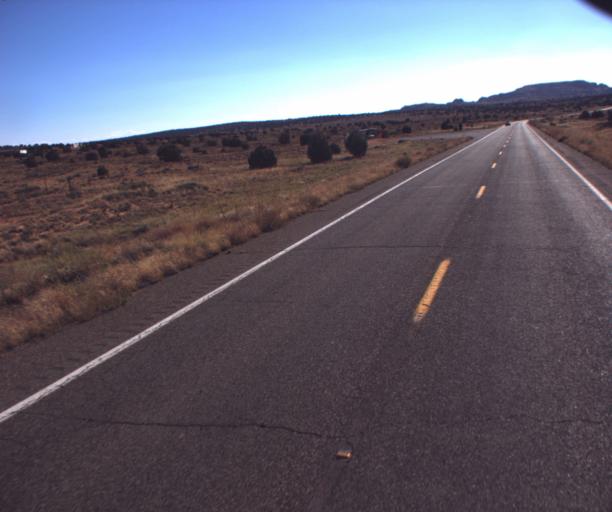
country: US
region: Arizona
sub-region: Coconino County
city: Kaibito
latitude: 36.5872
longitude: -111.1030
